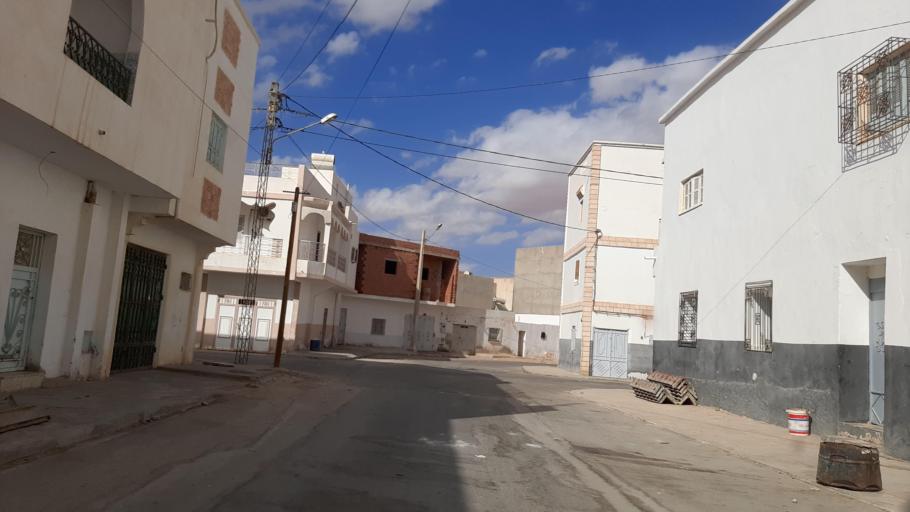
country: TN
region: Tataouine
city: Tataouine
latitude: 32.9279
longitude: 10.4538
